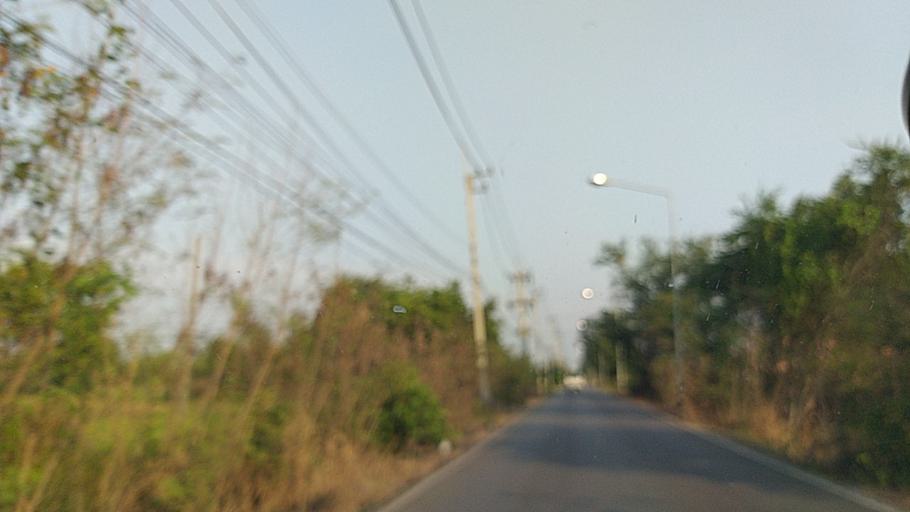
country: TH
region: Sara Buri
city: Nong Khae
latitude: 14.2823
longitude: 100.8162
